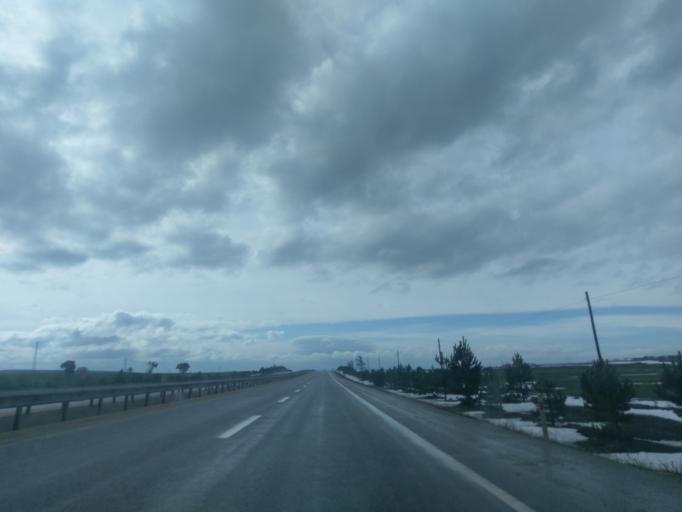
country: TR
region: Eskisehir
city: Inonu
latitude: 39.7234
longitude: 30.2629
